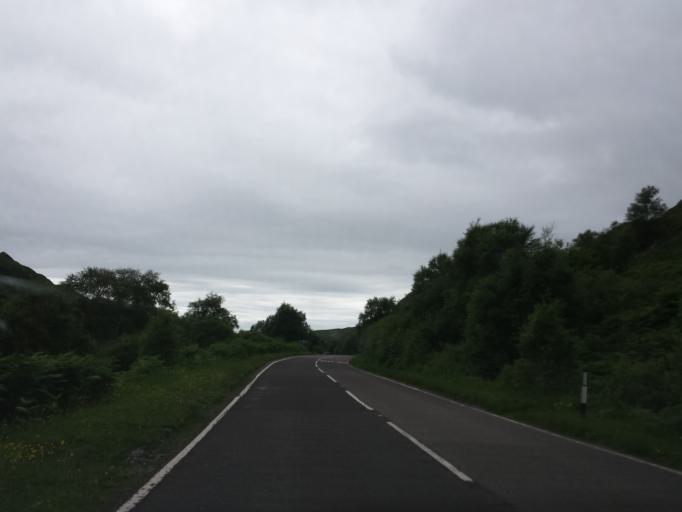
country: GB
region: Scotland
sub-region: Argyll and Bute
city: Isle Of Mull
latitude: 56.8870
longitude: -5.6386
